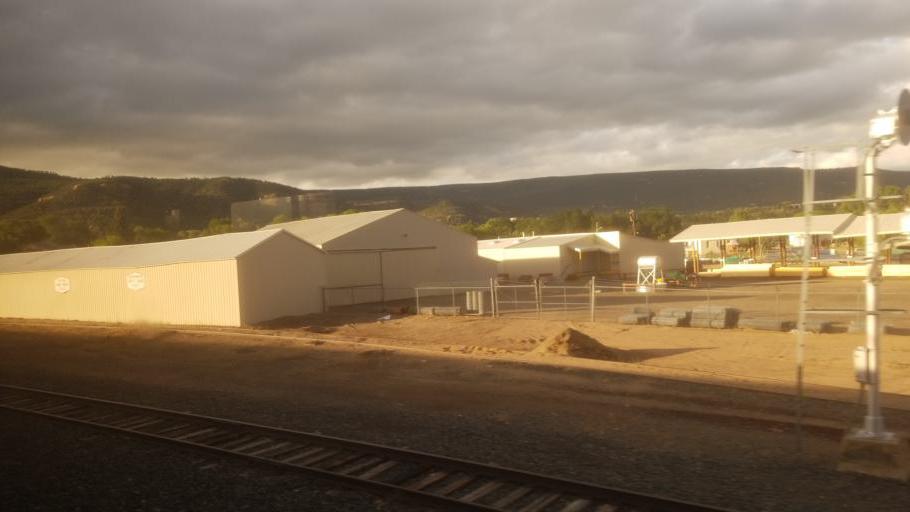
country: US
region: New Mexico
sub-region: Colfax County
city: Raton
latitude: 36.9041
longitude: -104.4380
